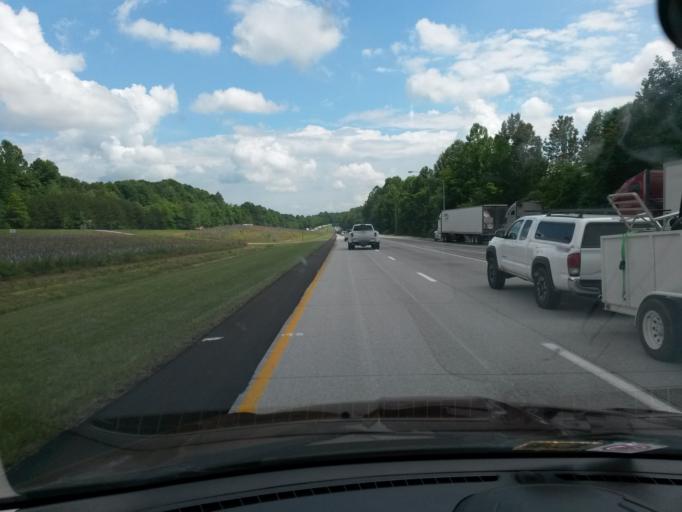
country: US
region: Virginia
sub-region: Carroll County
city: Cana
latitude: 36.5246
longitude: -80.7473
